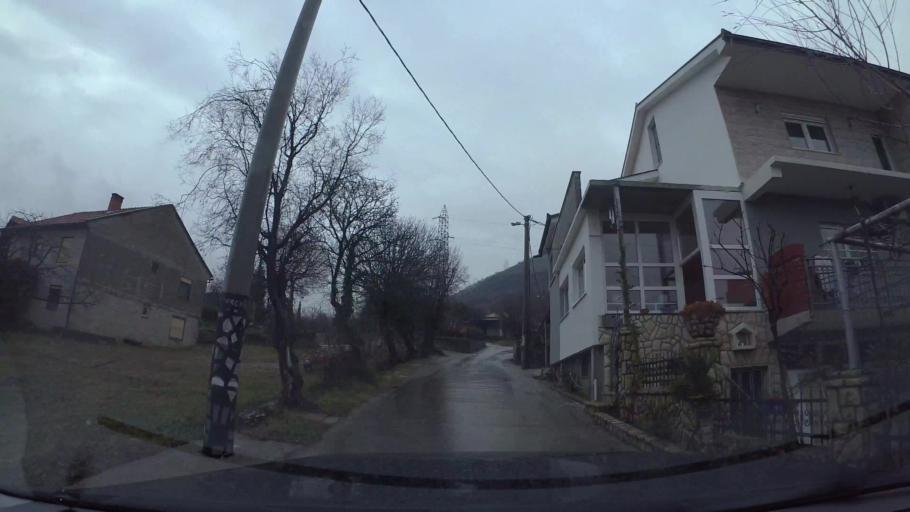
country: BA
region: Federation of Bosnia and Herzegovina
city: Cim
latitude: 43.3540
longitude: 17.7829
